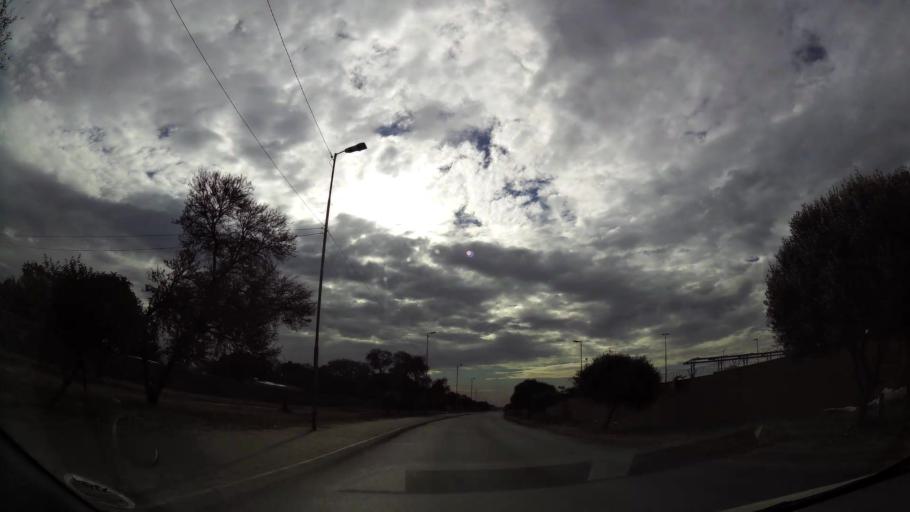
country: ZA
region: Gauteng
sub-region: City of Tshwane Metropolitan Municipality
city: Pretoria
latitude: -25.7266
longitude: 28.3131
